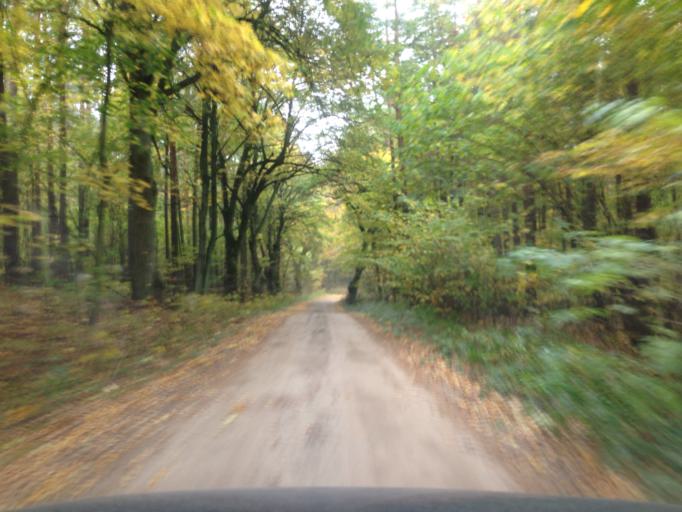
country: PL
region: Kujawsko-Pomorskie
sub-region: Powiat brodnicki
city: Bartniczka
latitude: 53.2637
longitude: 19.5809
